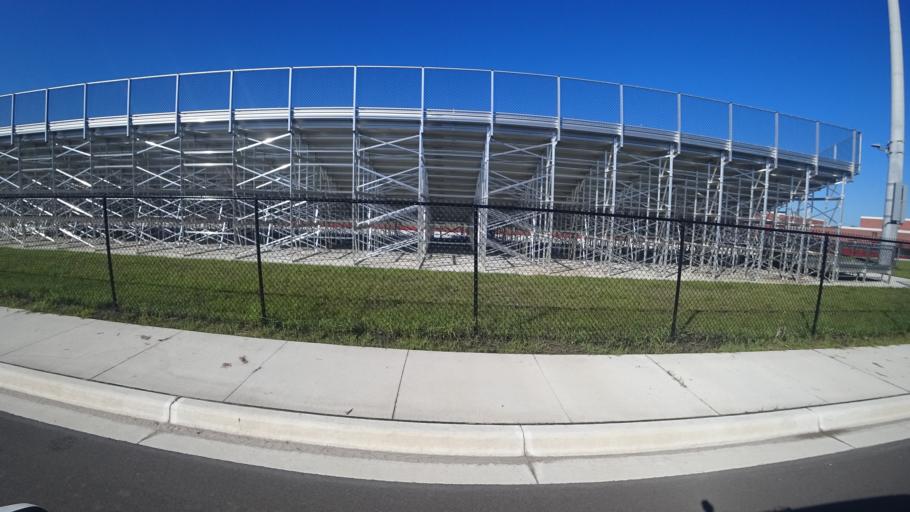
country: US
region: Florida
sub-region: Manatee County
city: Ellenton
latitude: 27.5795
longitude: -82.4378
